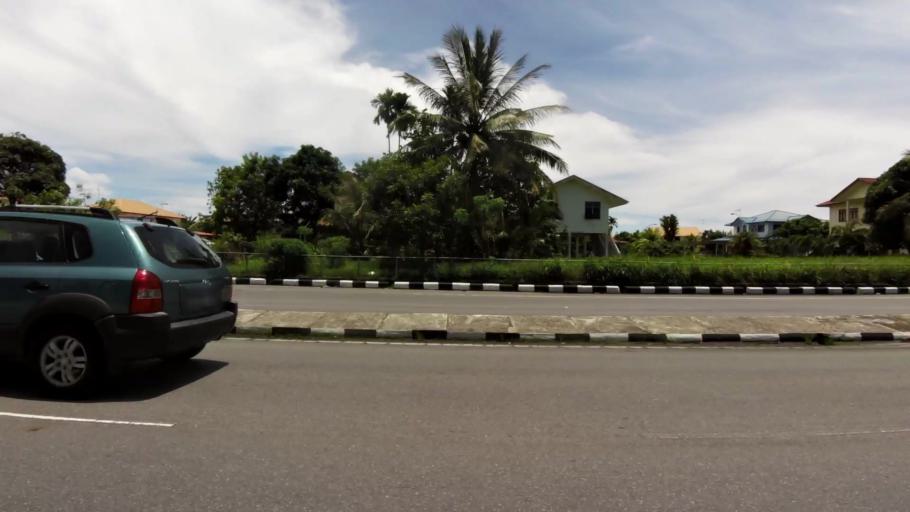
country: BN
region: Belait
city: Kuala Belait
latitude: 4.5841
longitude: 114.2430
